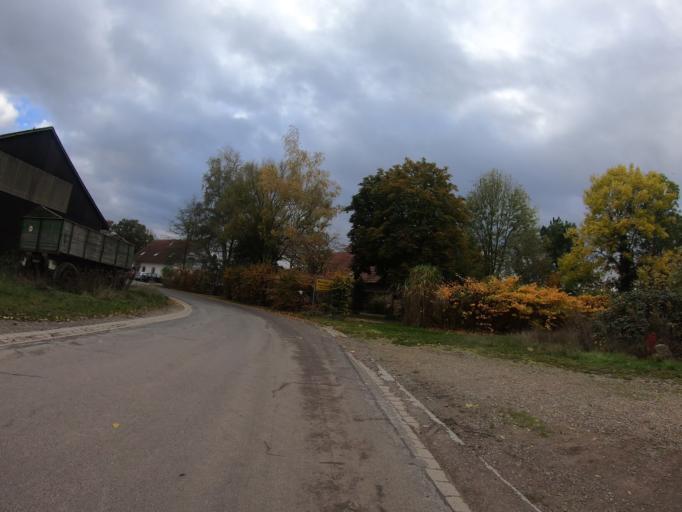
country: DE
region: Lower Saxony
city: Adenbuettel
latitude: 52.4033
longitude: 10.4727
